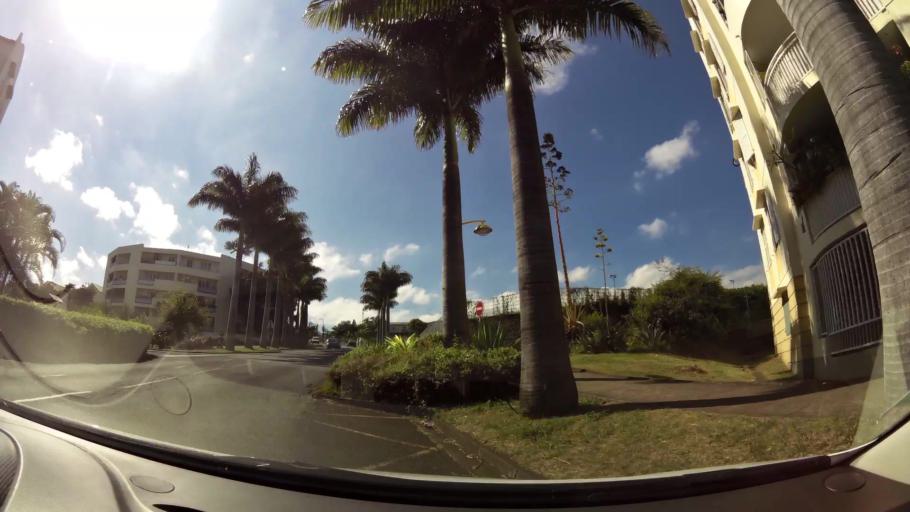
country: RE
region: Reunion
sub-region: Reunion
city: Le Tampon
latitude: -21.2762
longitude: 55.5044
